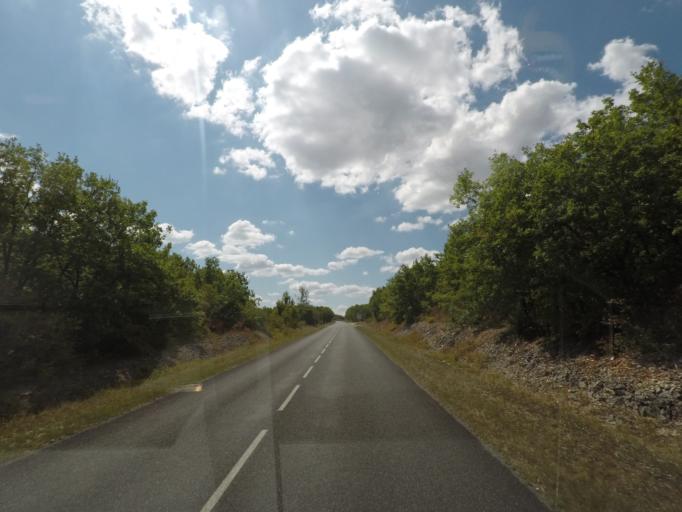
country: FR
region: Midi-Pyrenees
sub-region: Departement du Lot
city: Cajarc
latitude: 44.5794
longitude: 1.6930
